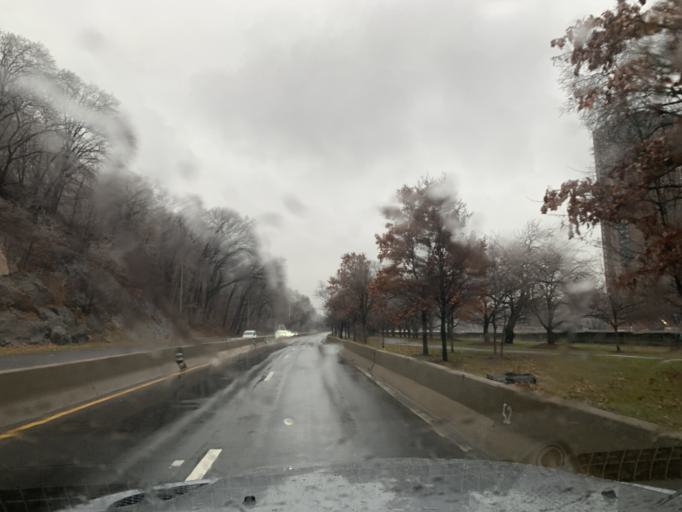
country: US
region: New York
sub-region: New York County
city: Inwood
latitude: 40.8508
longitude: -73.9262
